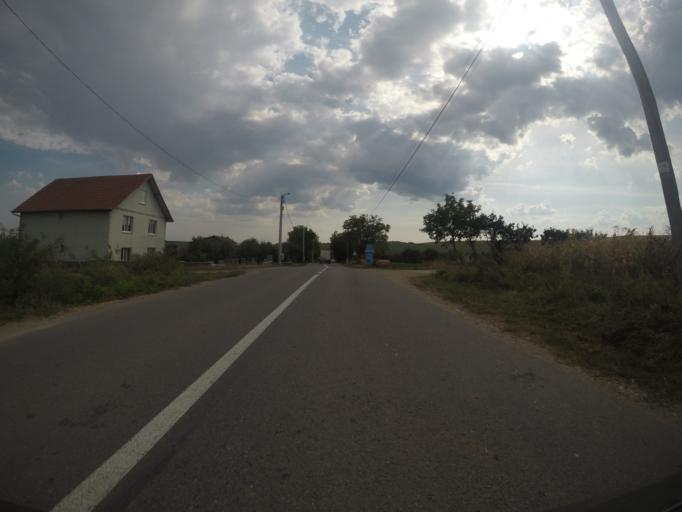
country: RO
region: Cluj
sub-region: Comuna Sandulesti
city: Sandulesti
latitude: 46.5821
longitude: 23.7314
